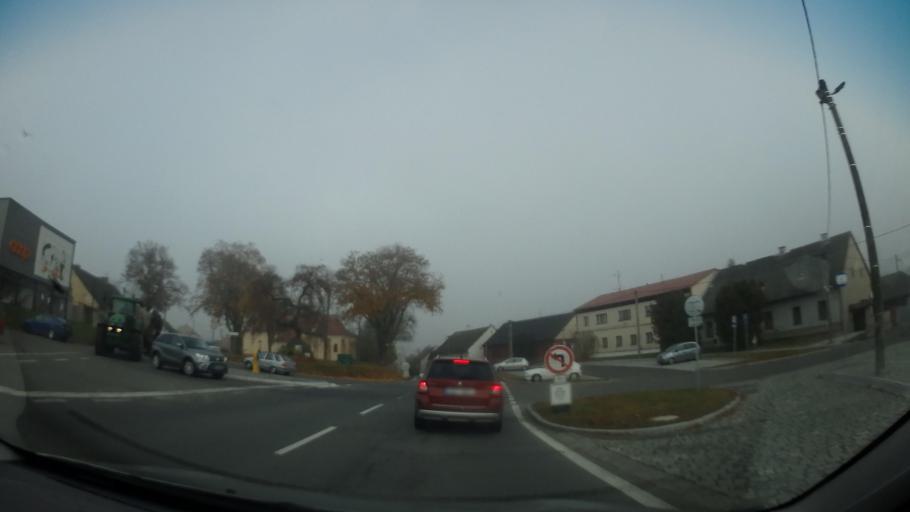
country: CZ
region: Vysocina
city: Krizanov
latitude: 49.4752
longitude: 16.1191
